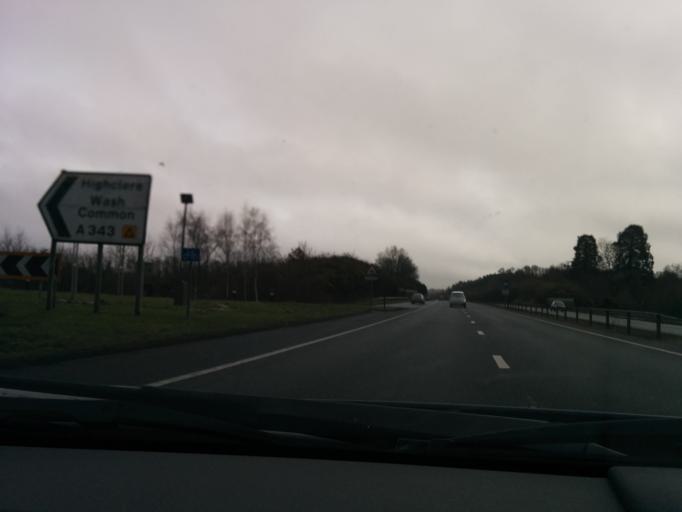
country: GB
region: England
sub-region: Hampshire
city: Highclere
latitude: 51.3638
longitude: -1.3590
